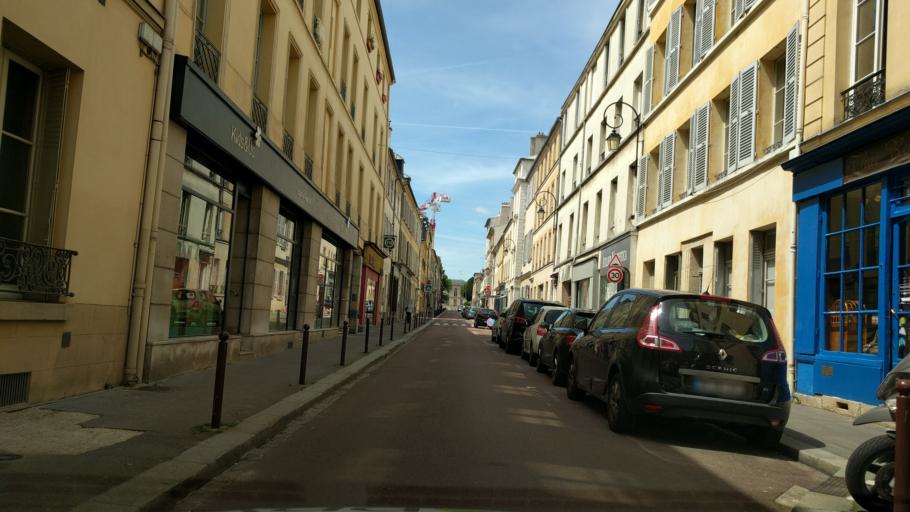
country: FR
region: Ile-de-France
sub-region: Departement des Yvelines
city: Versailles
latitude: 48.8007
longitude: 2.1236
